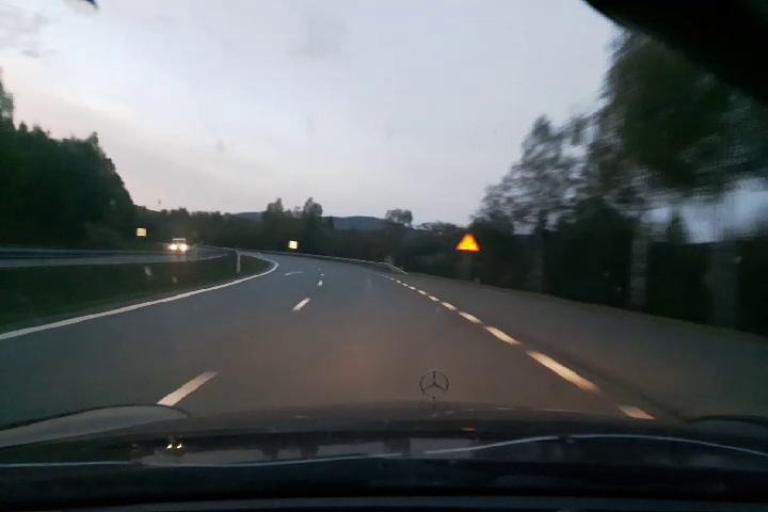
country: SE
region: Vaesternorrland
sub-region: Kramfors Kommun
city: Nordingra
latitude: 63.0126
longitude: 18.2903
